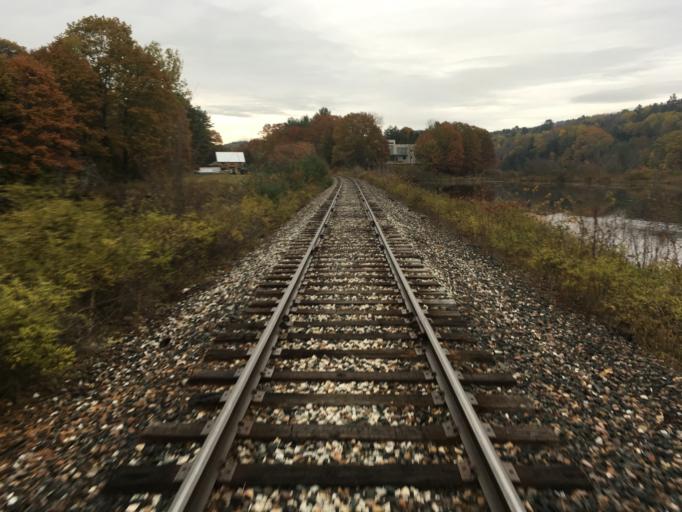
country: US
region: New Hampshire
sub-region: Grafton County
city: Hanover
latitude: 43.7478
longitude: -72.2351
